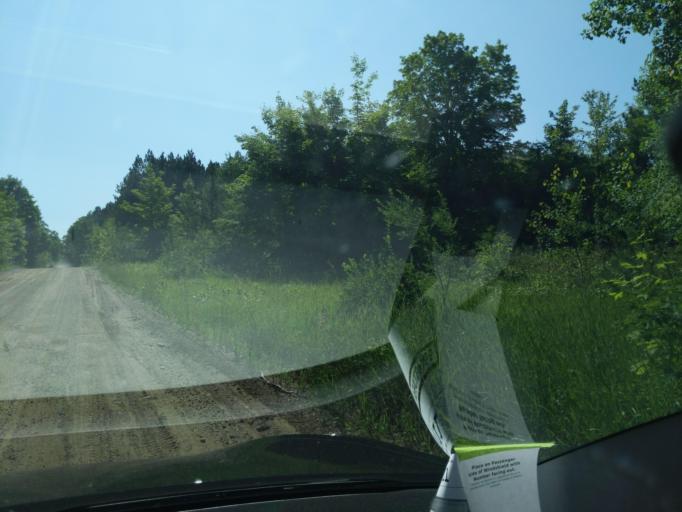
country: US
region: Michigan
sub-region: Mackinac County
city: Saint Ignace
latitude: 45.6793
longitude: -84.6751
